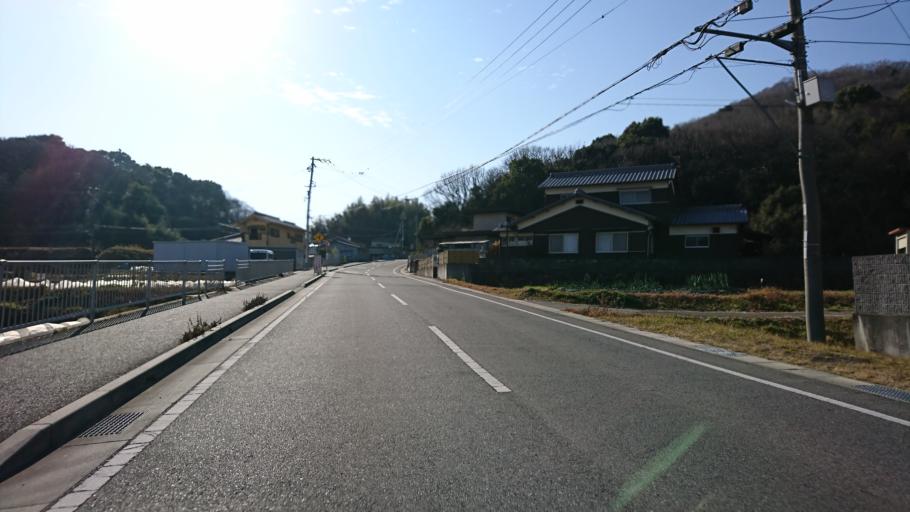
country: JP
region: Hyogo
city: Kakogawacho-honmachi
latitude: 34.8273
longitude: 134.8298
